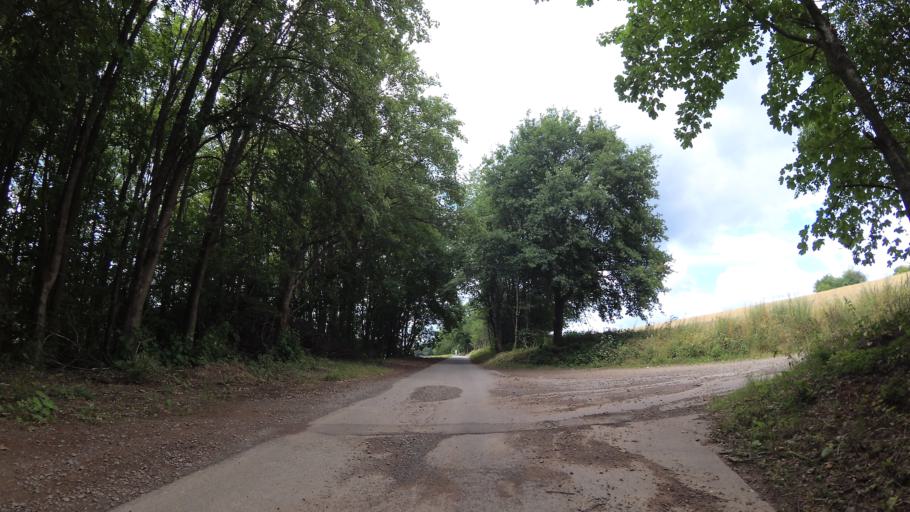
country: DE
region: Rheinland-Pfalz
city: Breitenbach
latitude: 49.4728
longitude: 7.2356
